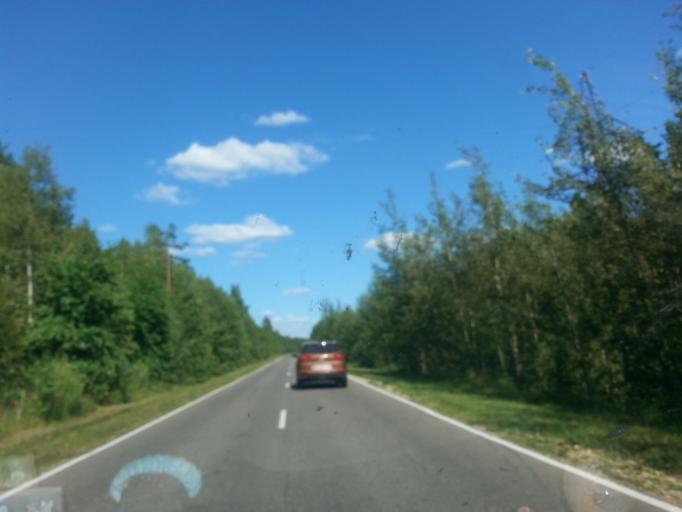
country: RU
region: Nizjnij Novgorod
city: Taremskoye
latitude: 56.0102
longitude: 42.9276
